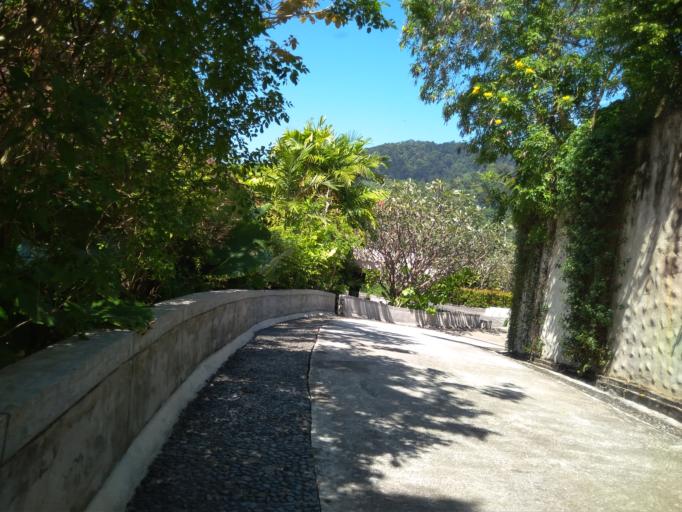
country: TH
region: Krabi
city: Ko Lanta
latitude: 7.4962
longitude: 99.0782
